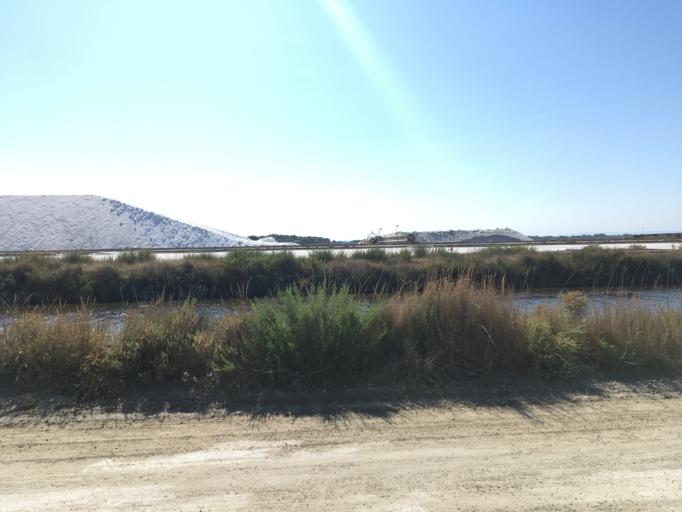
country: FR
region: Languedoc-Roussillon
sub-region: Departement du Gard
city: Aigues-Mortes
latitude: 43.5495
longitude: 4.1869
